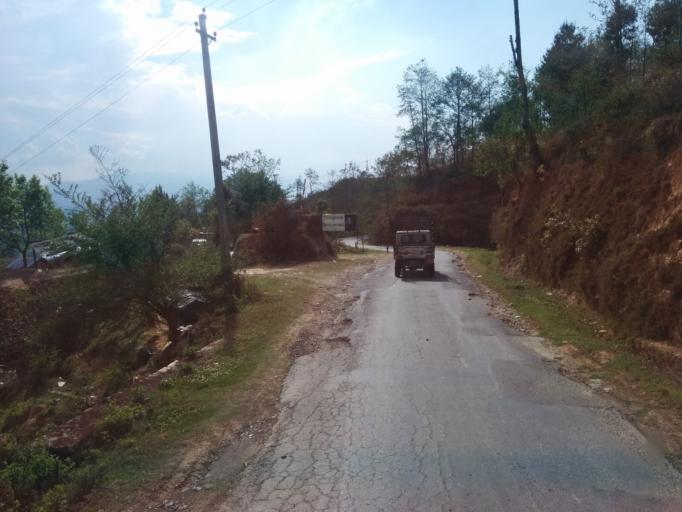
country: NP
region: Central Region
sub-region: Bagmati Zone
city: Nagarkot
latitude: 27.7097
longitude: 85.5045
